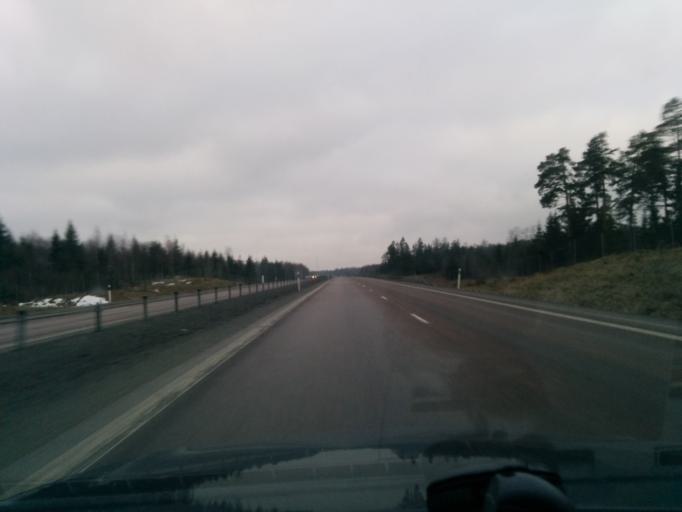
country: SE
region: Uppsala
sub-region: Enkopings Kommun
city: Hummelsta
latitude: 59.6399
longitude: 16.9230
